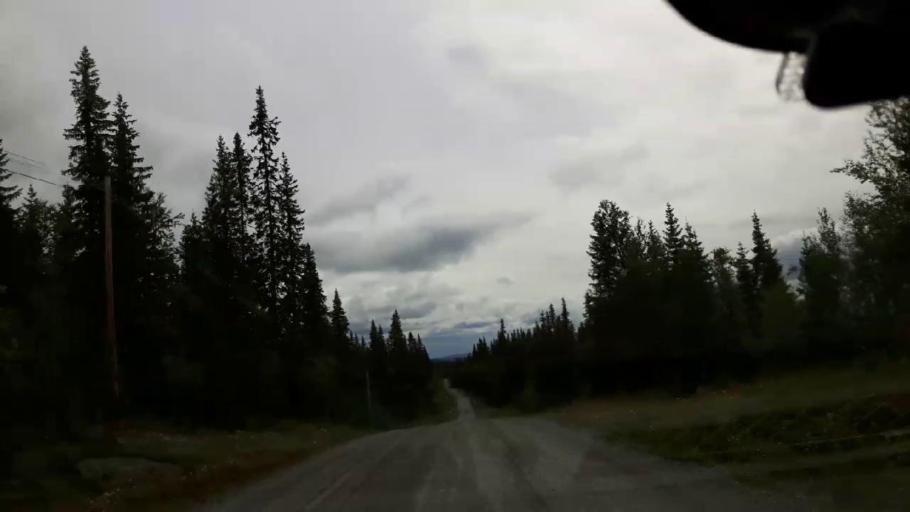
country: SE
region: Jaemtland
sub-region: Krokoms Kommun
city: Valla
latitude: 63.7246
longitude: 13.8468
